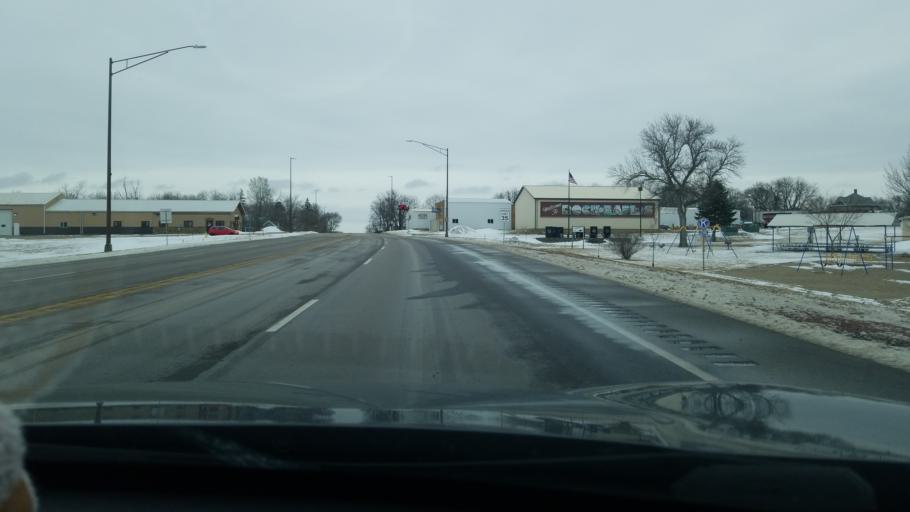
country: US
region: Iowa
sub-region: Lyon County
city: Rock Rapids
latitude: 43.4320
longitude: -96.1824
